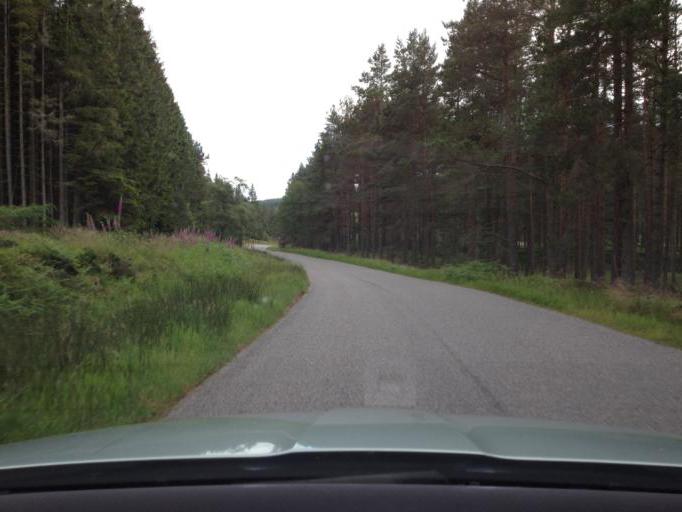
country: GB
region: Scotland
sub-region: Aberdeenshire
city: Banchory
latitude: 56.9943
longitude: -2.5750
